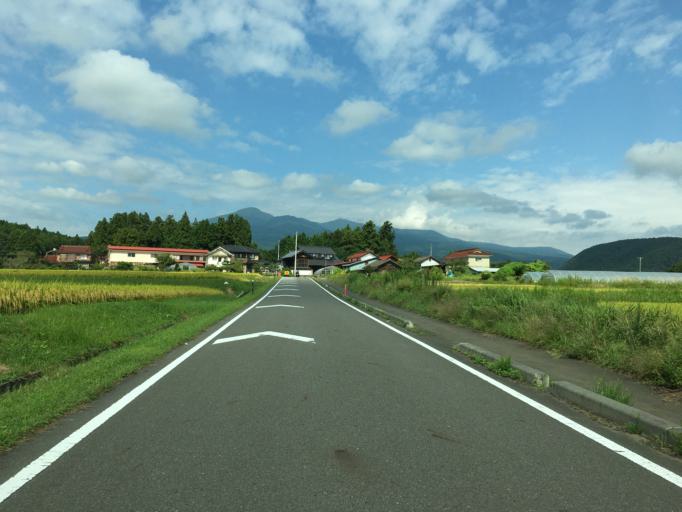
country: JP
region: Fukushima
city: Motomiya
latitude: 37.5408
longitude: 140.3622
